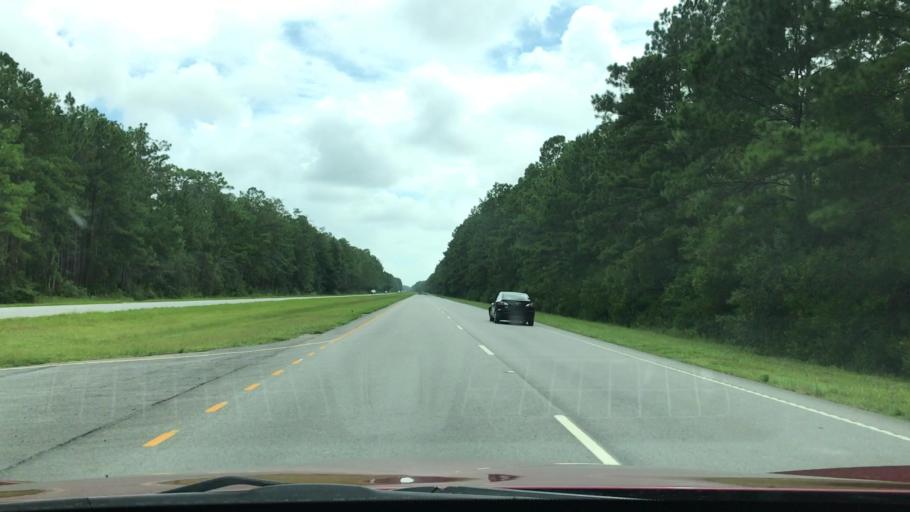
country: US
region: South Carolina
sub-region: Charleston County
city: Awendaw
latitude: 33.1450
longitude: -79.4370
